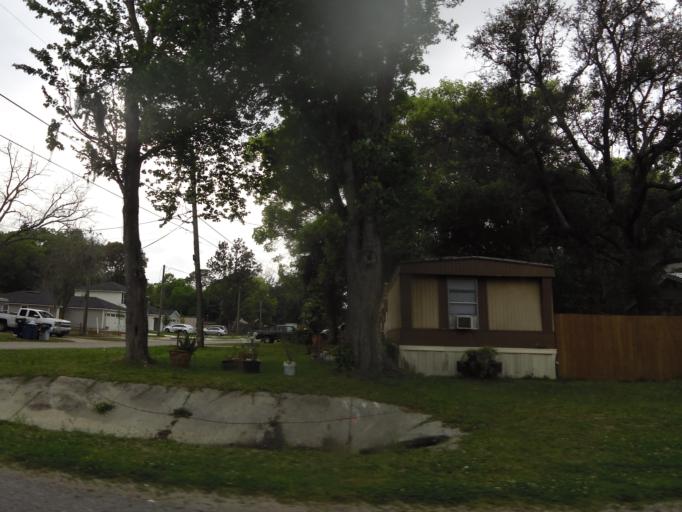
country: US
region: Florida
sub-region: Duval County
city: Jacksonville
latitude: 30.3183
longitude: -81.5660
